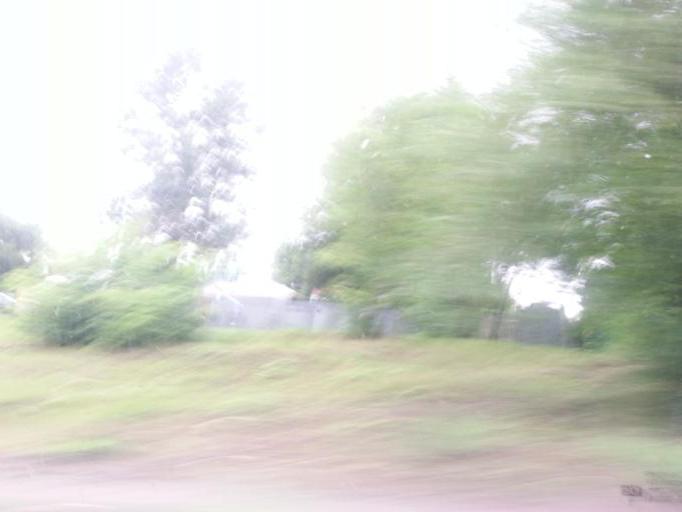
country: RU
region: Tatarstan
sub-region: Gorod Kazan'
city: Kazan
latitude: 55.7648
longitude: 49.2025
